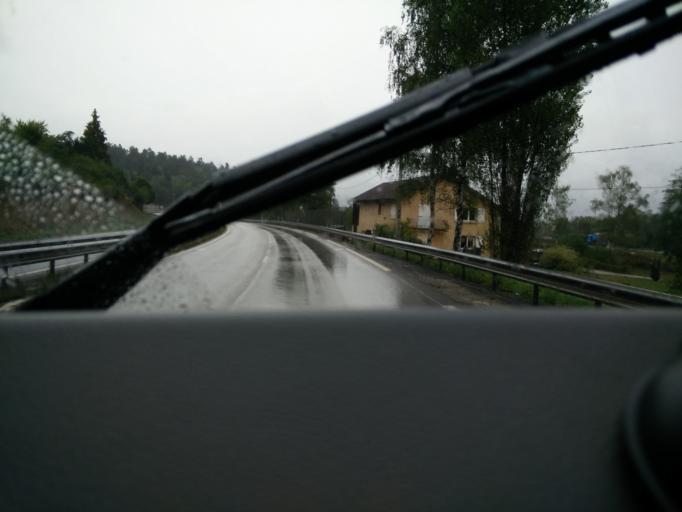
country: FR
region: Lorraine
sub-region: Departement des Vosges
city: Saulcy-sur-Meurthe
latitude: 48.2525
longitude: 6.9584
